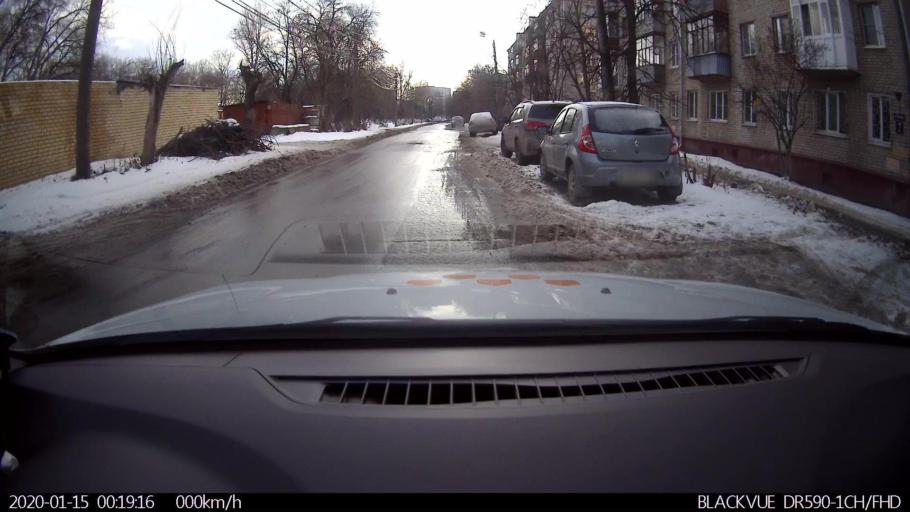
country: RU
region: Nizjnij Novgorod
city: Gorbatovka
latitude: 56.2467
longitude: 43.8684
